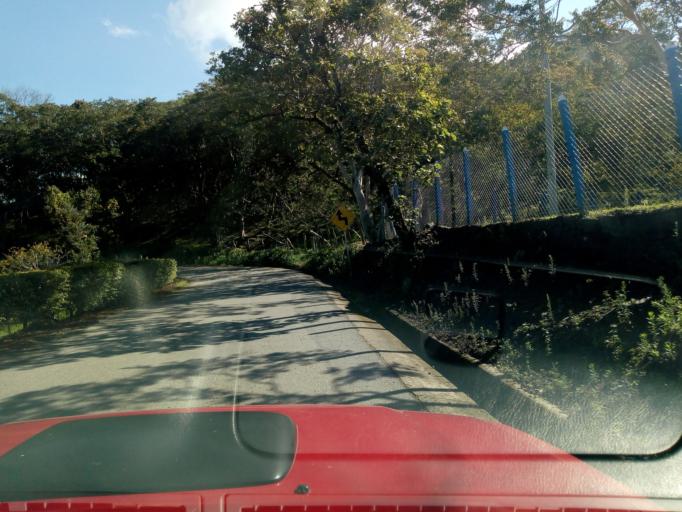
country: CO
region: Boyaca
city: Moniquira
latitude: 5.8766
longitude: -73.5505
